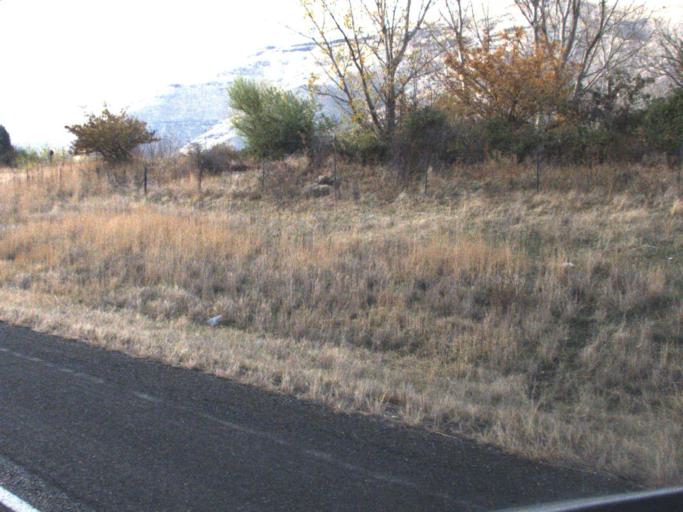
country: US
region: Washington
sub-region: Asotin County
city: Clarkston Heights-Vineland
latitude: 46.4248
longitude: -117.1612
